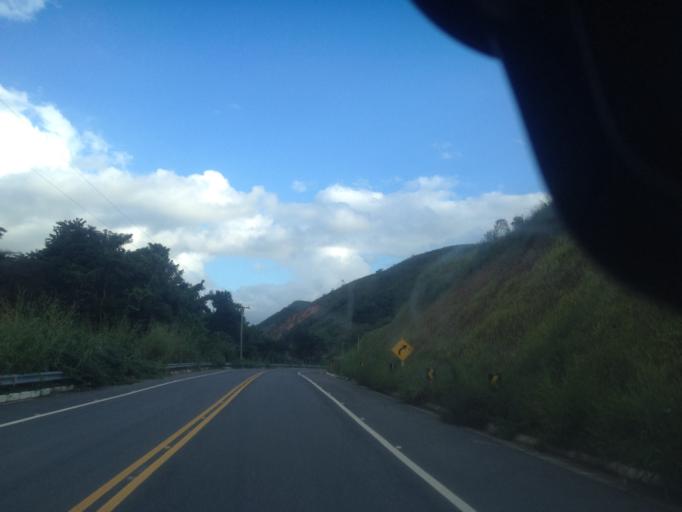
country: BR
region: Rio de Janeiro
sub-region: Quatis
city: Quatis
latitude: -22.2755
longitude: -44.2583
